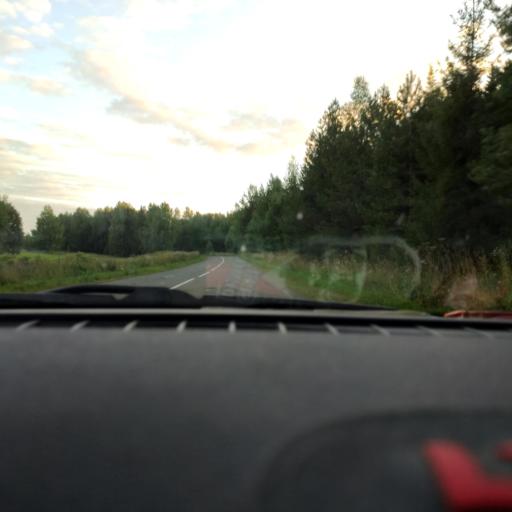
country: RU
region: Perm
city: Ocher
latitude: 57.9359
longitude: 54.7960
